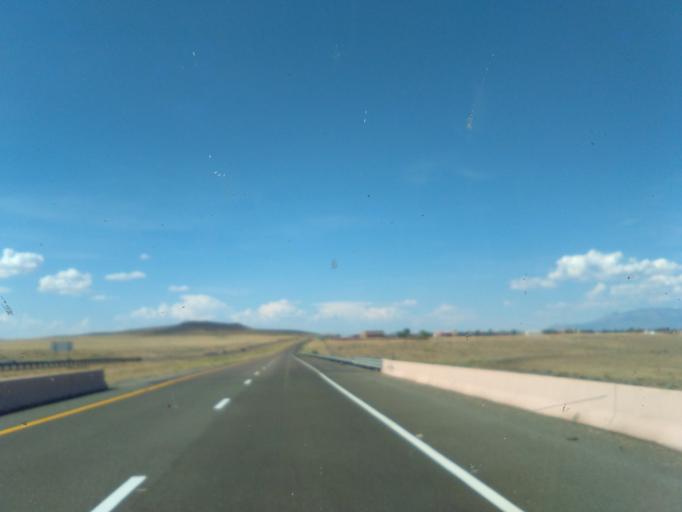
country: US
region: New Mexico
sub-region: Valencia County
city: Bosque Farms
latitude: 34.8896
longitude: -106.7272
